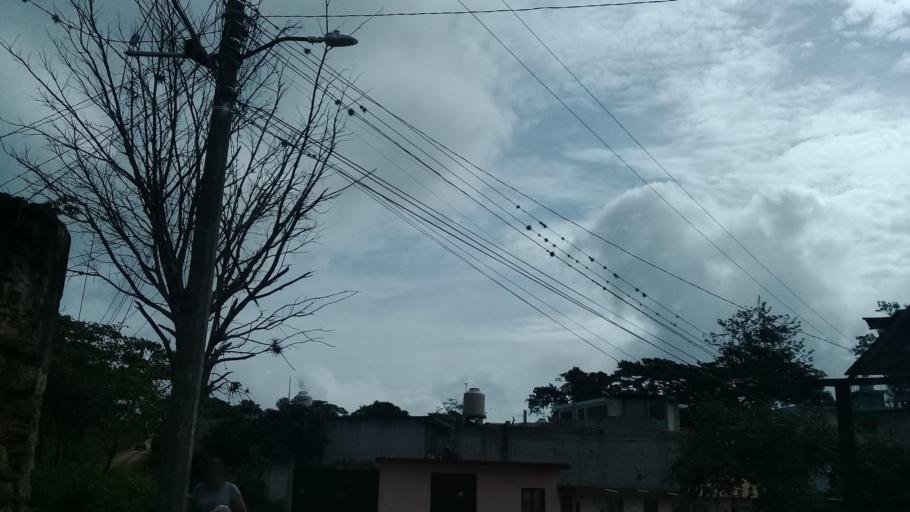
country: MX
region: Veracruz
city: El Castillo
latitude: 19.5496
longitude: -96.8771
